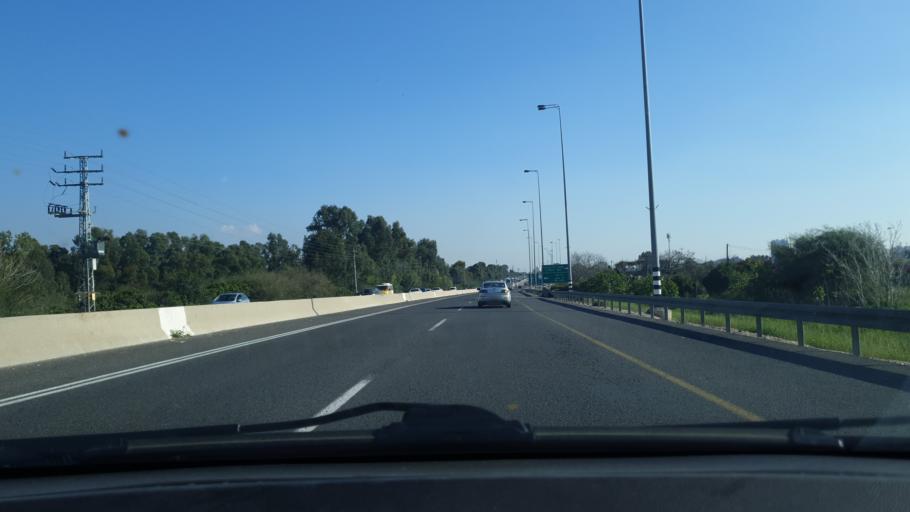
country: IL
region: Central District
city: Ramla
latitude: 31.9571
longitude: 34.8535
